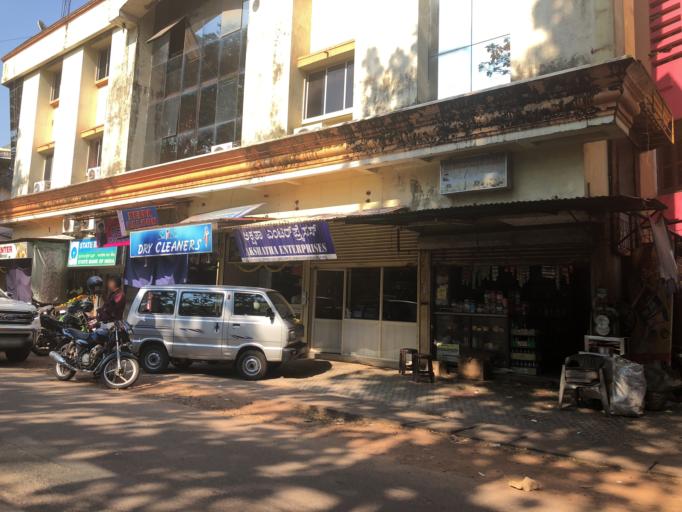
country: IN
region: Karnataka
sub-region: Dakshina Kannada
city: Mangalore
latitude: 12.8841
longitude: 74.8332
